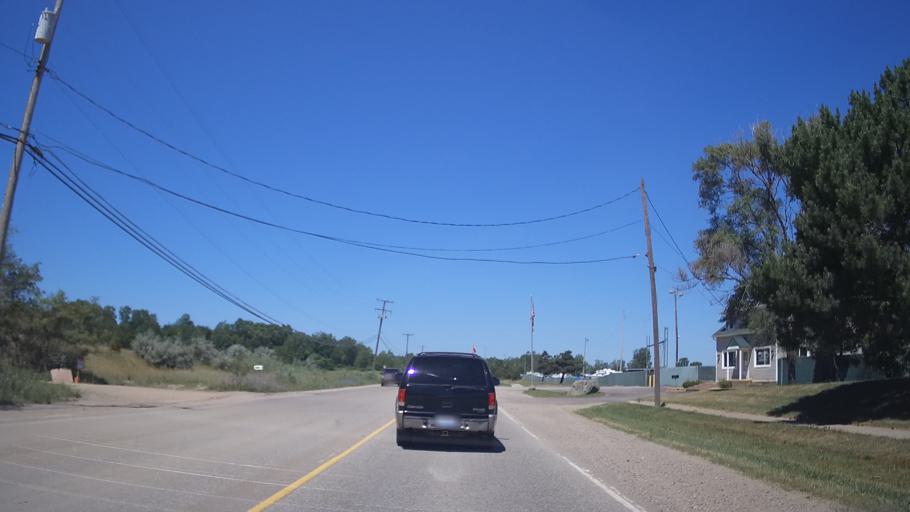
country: US
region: Michigan
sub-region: Macomb County
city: Shelby
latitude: 42.6510
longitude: -83.0749
